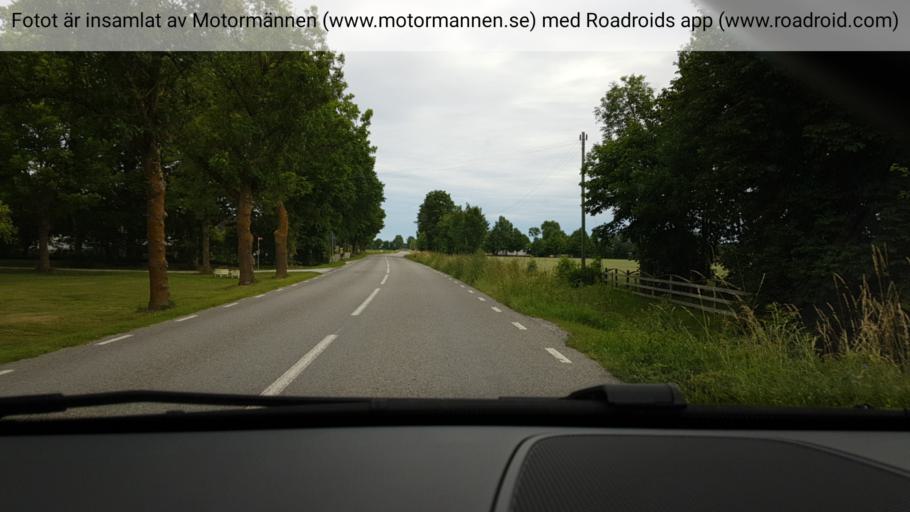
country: SE
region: Gotland
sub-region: Gotland
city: Hemse
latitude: 57.2192
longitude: 18.2180
